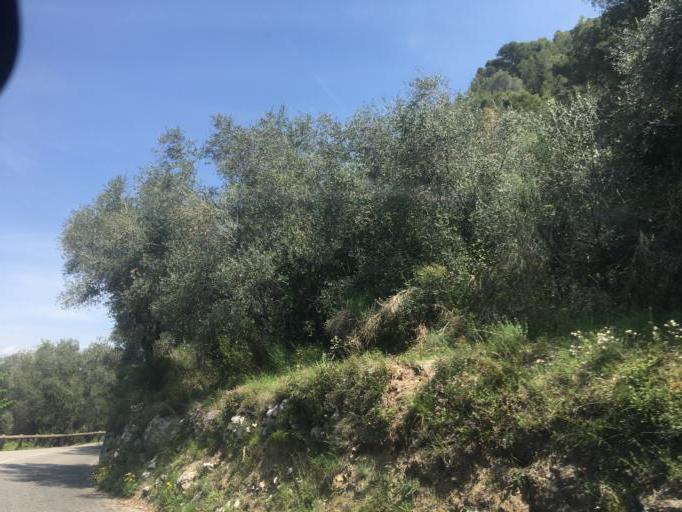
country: FR
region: Provence-Alpes-Cote d'Azur
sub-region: Departement des Alpes-Maritimes
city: Saint-Martin-du-Var
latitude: 43.8256
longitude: 7.1923
